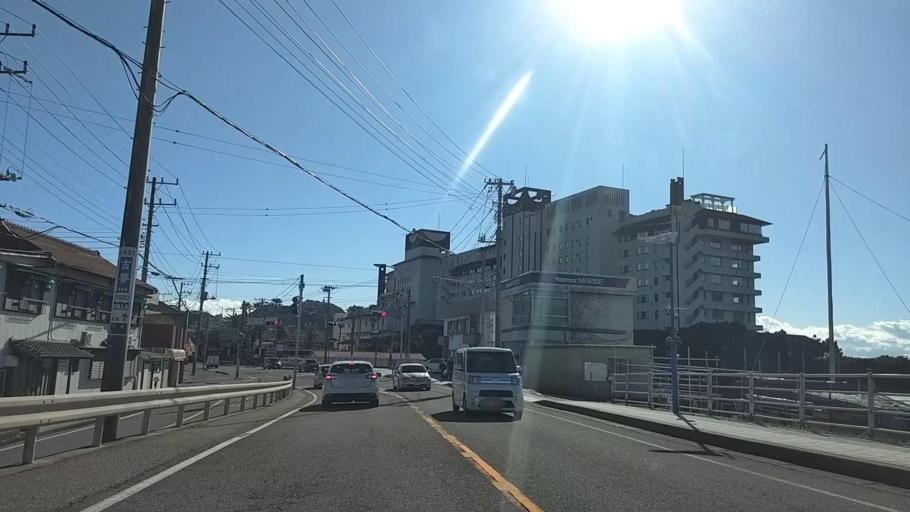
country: JP
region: Chiba
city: Kawaguchi
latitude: 35.1260
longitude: 140.1944
